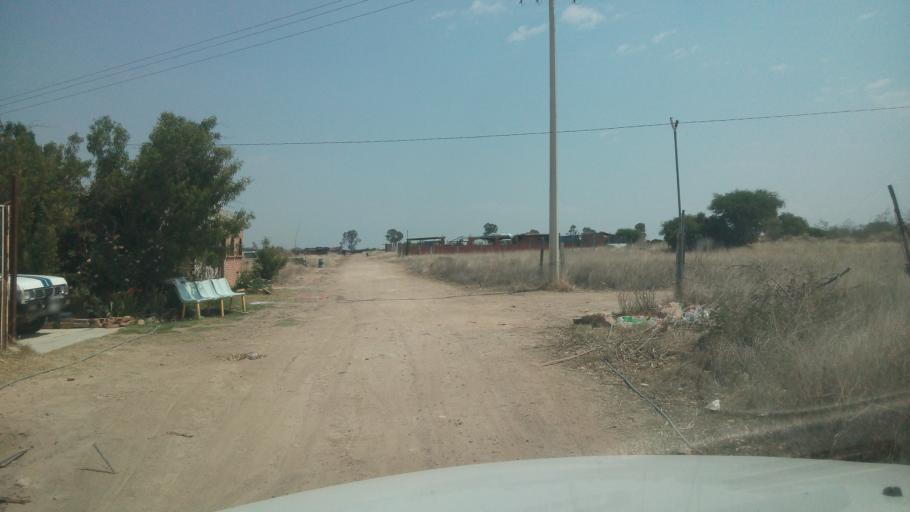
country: MX
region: Aguascalientes
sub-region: Aguascalientes
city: Villa Licenciado Jesus Teran (Calvillito)
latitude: 21.8439
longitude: -102.1649
